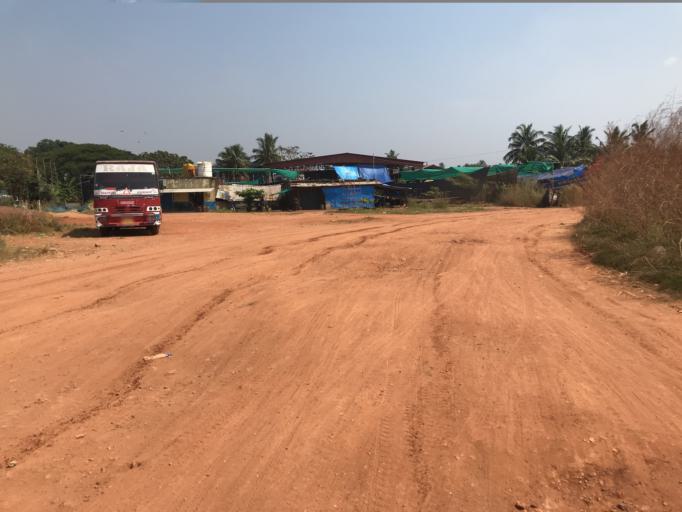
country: IN
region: Karnataka
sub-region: Dakshina Kannada
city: Ullal
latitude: 12.8511
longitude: 74.8343
